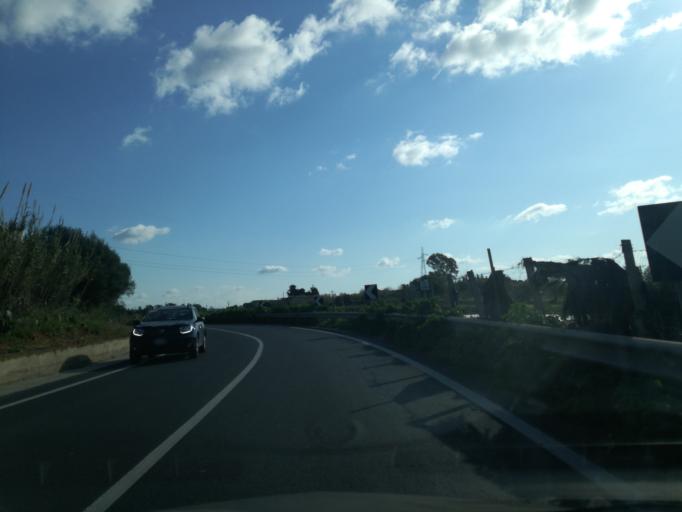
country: IT
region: Sicily
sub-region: Ragusa
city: Acate
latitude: 36.9942
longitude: 14.4333
